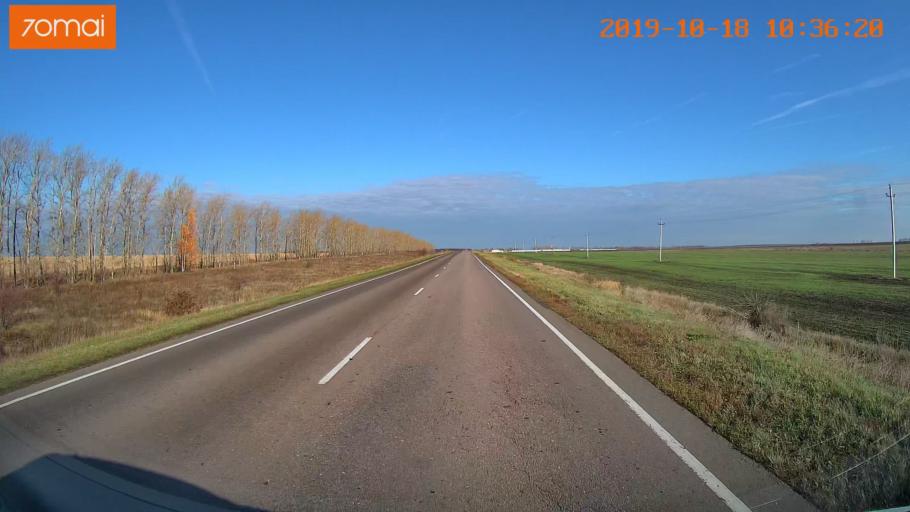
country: RU
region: Tula
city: Kurkino
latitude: 53.5466
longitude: 38.6250
